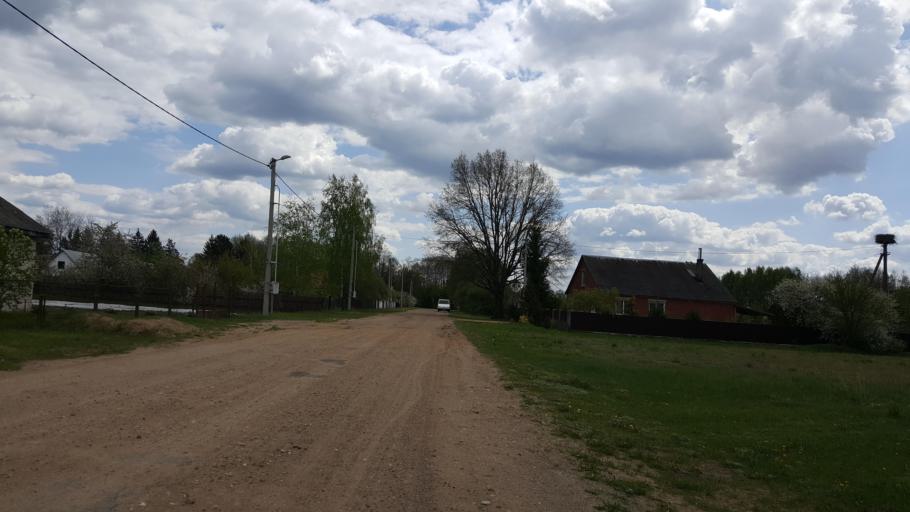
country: BY
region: Brest
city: Zhabinka
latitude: 52.3931
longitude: 24.0095
